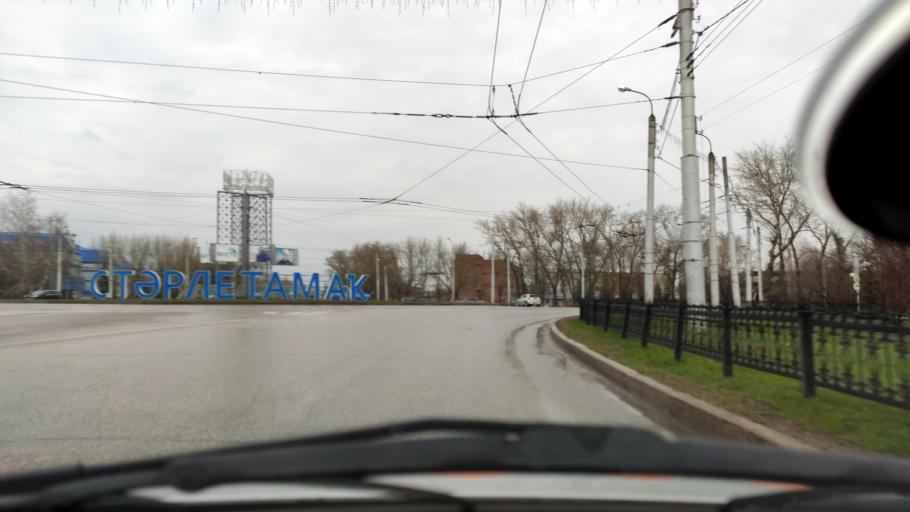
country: RU
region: Bashkortostan
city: Sterlitamak
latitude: 53.6625
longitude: 55.9491
